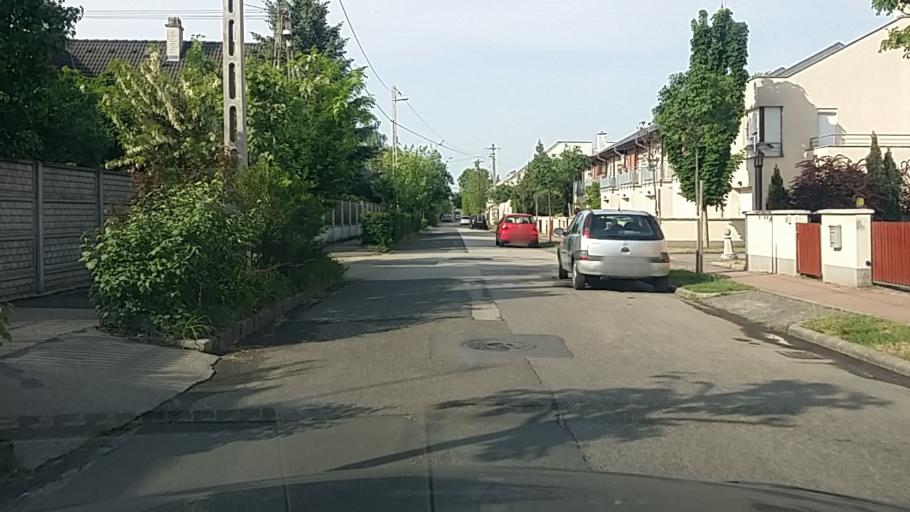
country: HU
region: Budapest
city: Budapest IV. keruelet
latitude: 47.5717
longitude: 19.0931
